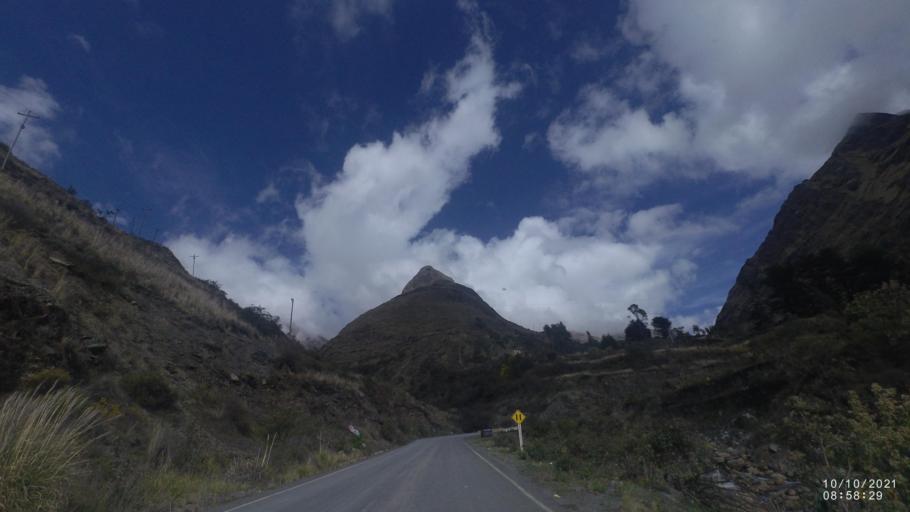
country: BO
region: La Paz
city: Quime
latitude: -16.9985
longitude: -67.2581
